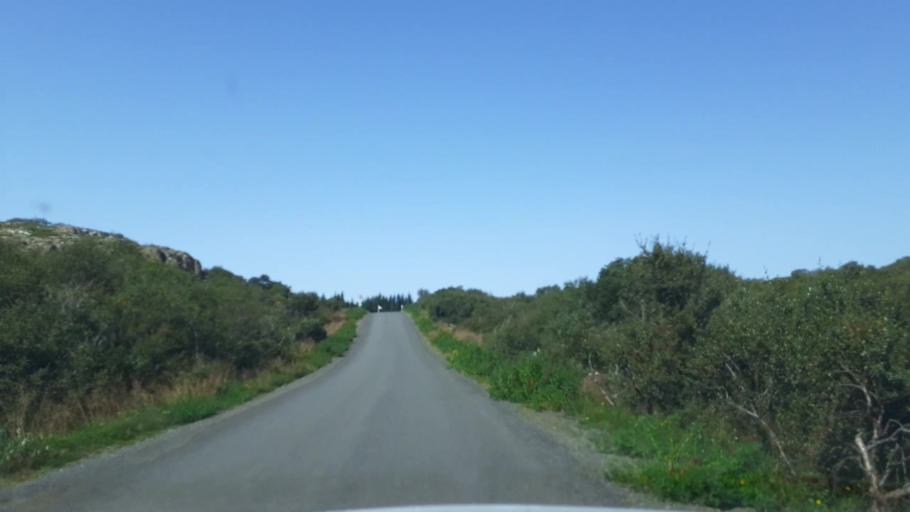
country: IS
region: West
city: Borgarnes
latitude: 64.7012
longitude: -21.6236
